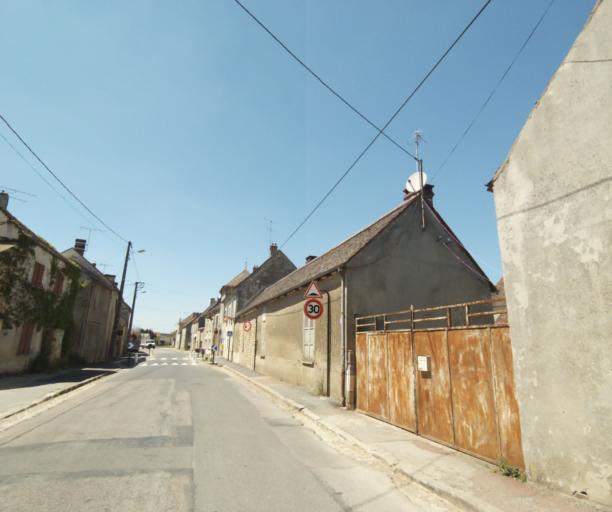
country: FR
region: Ile-de-France
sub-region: Departement de Seine-et-Marne
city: Noisy-sur-Ecole
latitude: 48.3467
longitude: 2.4572
